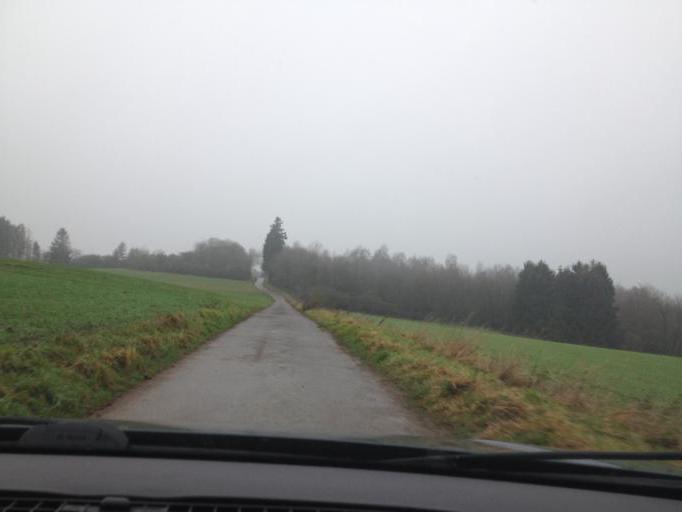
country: DE
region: Saarland
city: Marpingen
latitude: 49.4562
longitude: 7.0810
